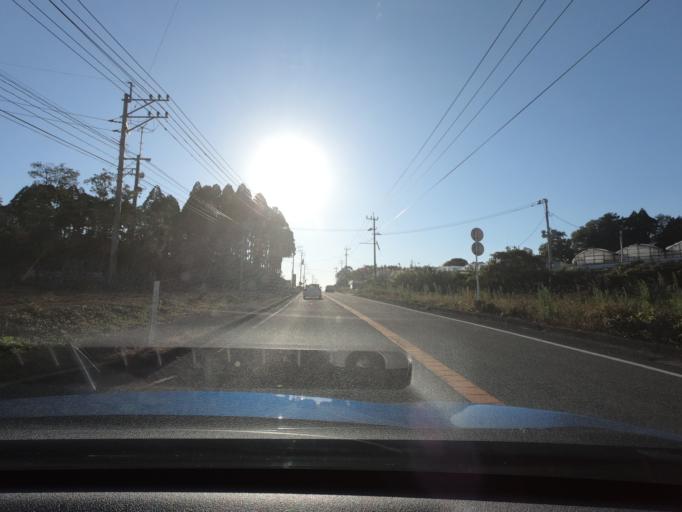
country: JP
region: Kagoshima
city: Akune
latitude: 32.0761
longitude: 130.2530
